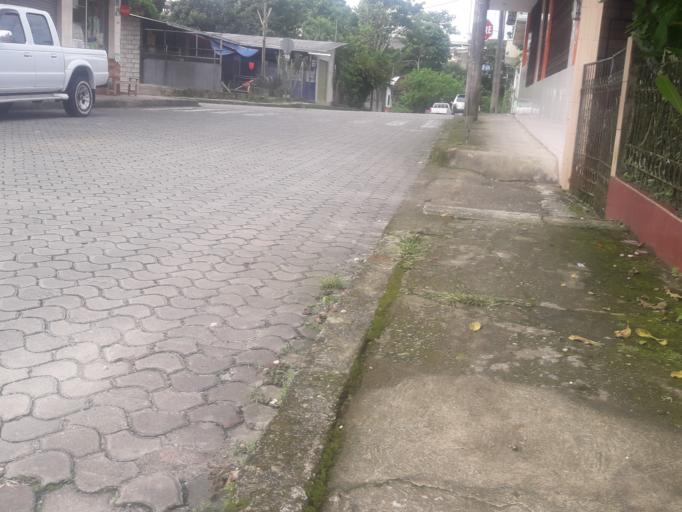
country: EC
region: Napo
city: Tena
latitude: -0.9942
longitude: -77.8103
